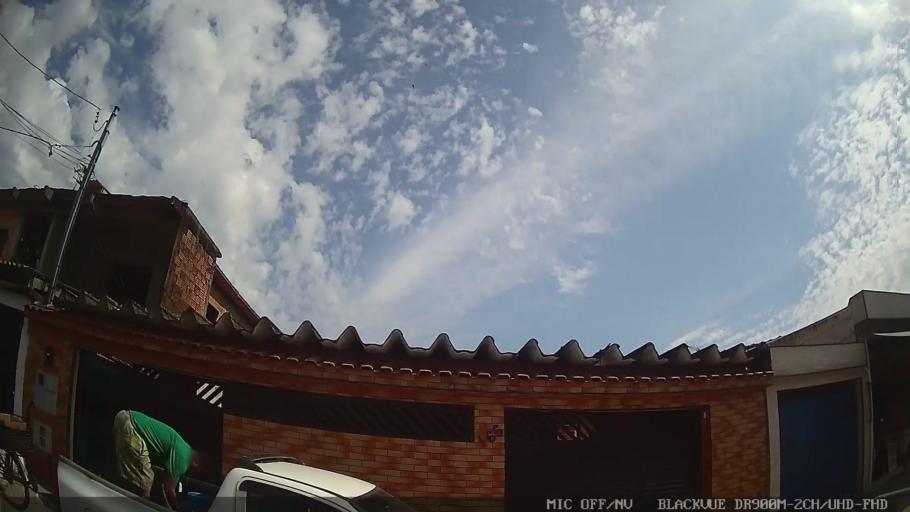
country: BR
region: Sao Paulo
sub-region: Santos
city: Santos
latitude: -23.9427
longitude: -46.2876
